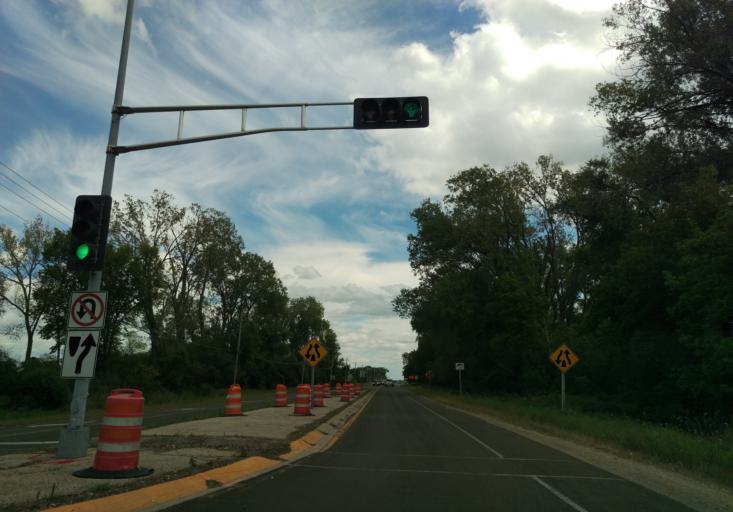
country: US
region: Wisconsin
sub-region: Dane County
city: Waunakee
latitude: 43.1477
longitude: -89.4322
